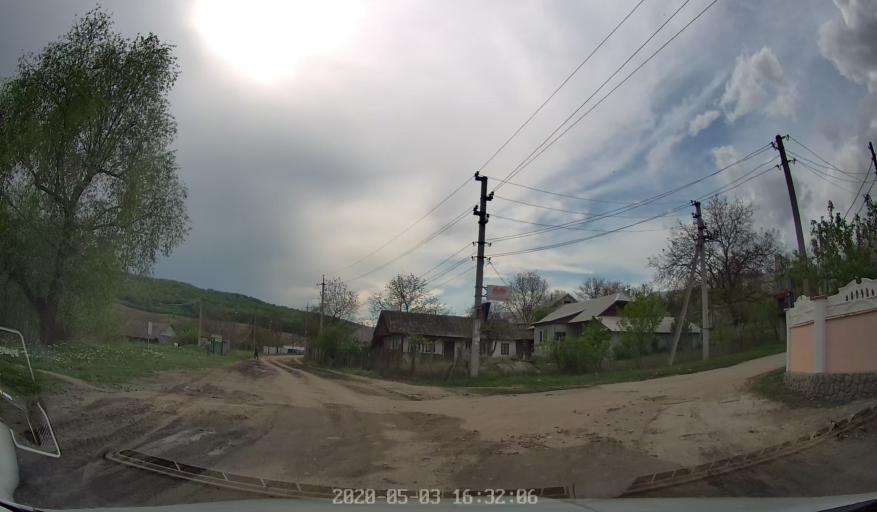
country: MD
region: Calarasi
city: Calarasi
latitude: 47.1922
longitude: 28.3359
